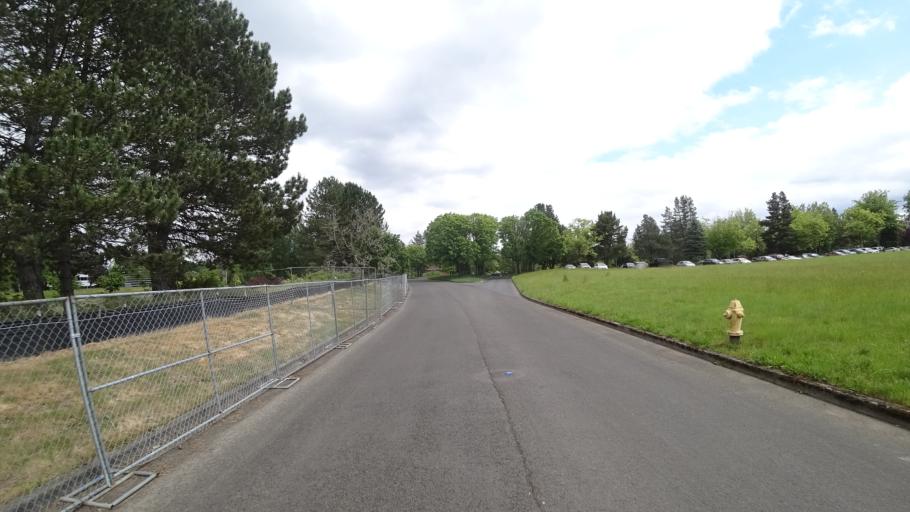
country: US
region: Oregon
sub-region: Washington County
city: Rockcreek
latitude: 45.5289
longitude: -122.8813
